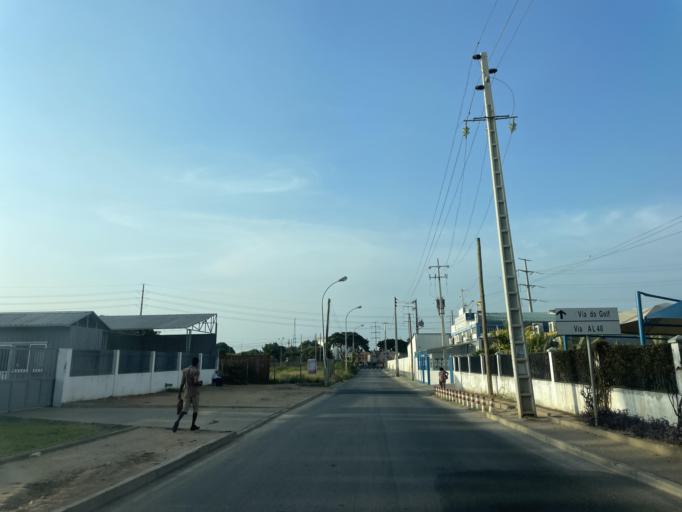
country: AO
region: Luanda
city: Luanda
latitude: -8.9076
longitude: 13.1840
